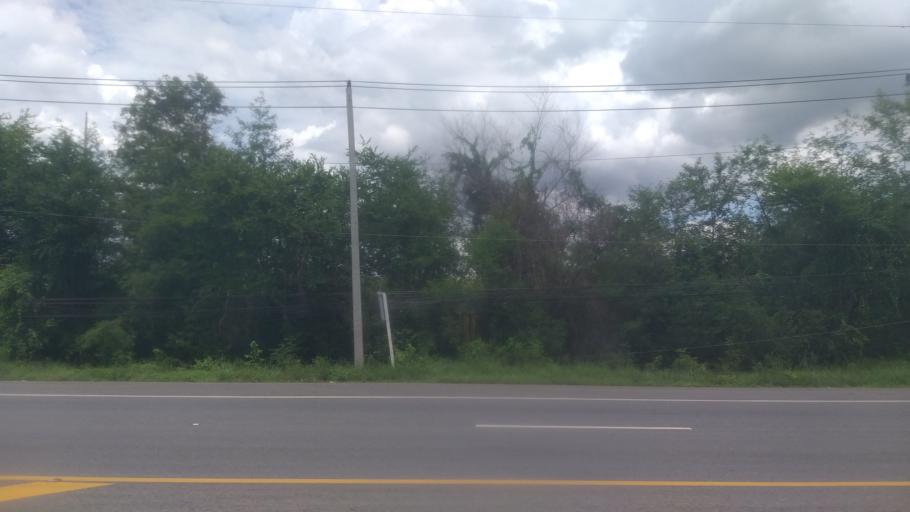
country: TH
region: Nakhon Ratchasima
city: Non Thai
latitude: 15.1112
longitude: 102.1013
